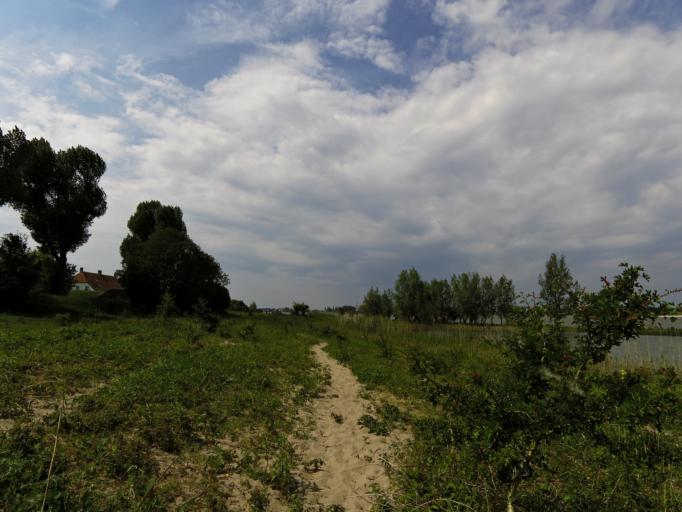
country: NL
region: North Brabant
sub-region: Gemeente Woudrichem
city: Woudrichem
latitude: 51.8166
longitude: 5.0249
